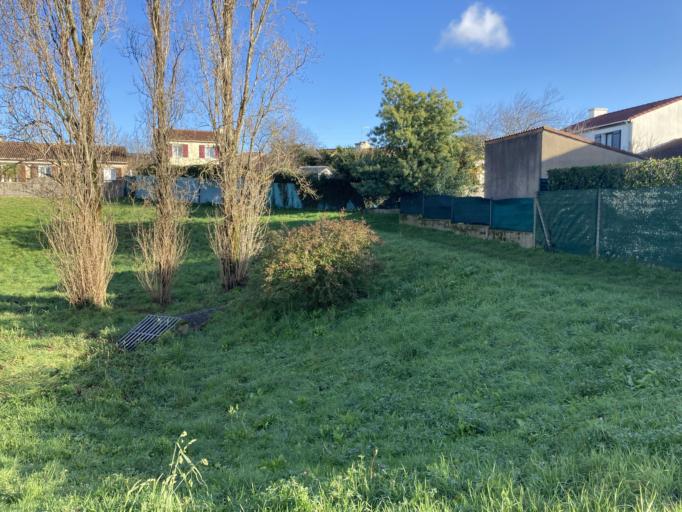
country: FR
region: Pays de la Loire
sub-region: Departement de la Loire-Atlantique
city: Saint-Sebastien-sur-Loire
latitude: 47.2030
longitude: -1.4888
